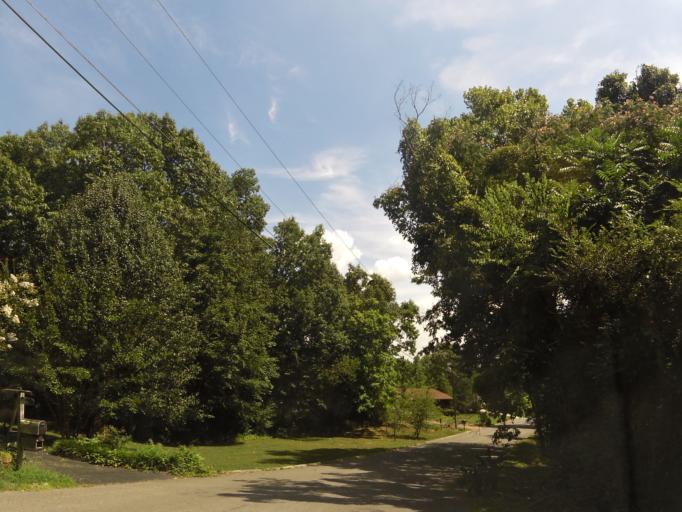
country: US
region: Tennessee
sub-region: Knox County
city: Knoxville
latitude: 35.9215
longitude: -83.8309
